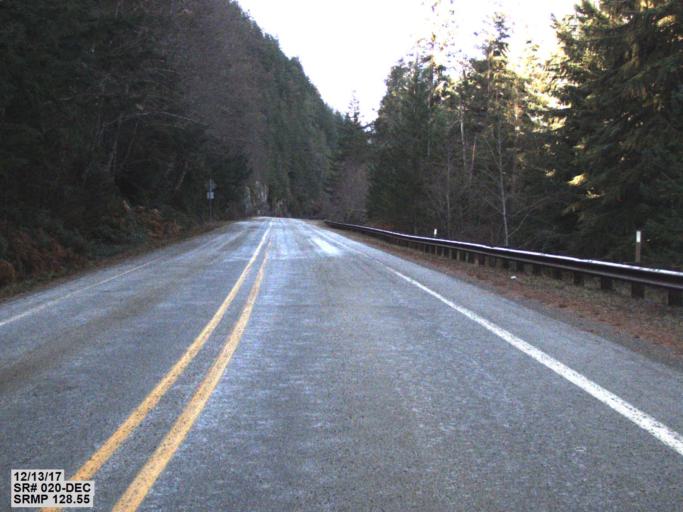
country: US
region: Washington
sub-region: Snohomish County
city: Darrington
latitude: 48.7076
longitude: -121.1154
